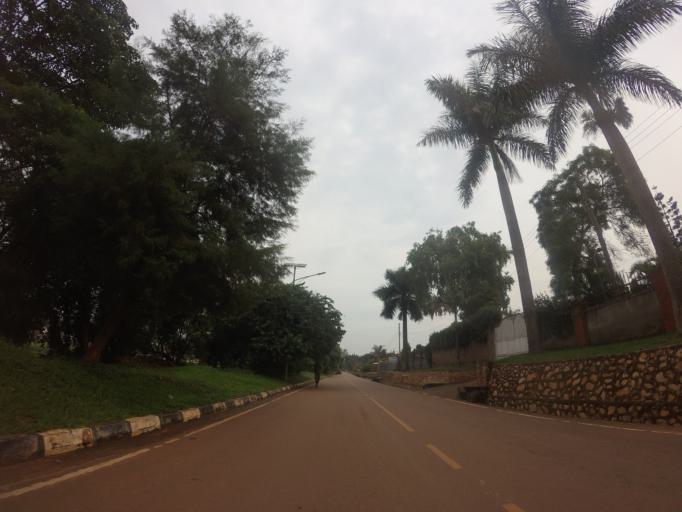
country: UG
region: Central Region
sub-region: Wakiso District
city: Kireka
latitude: 0.3500
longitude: 32.6219
